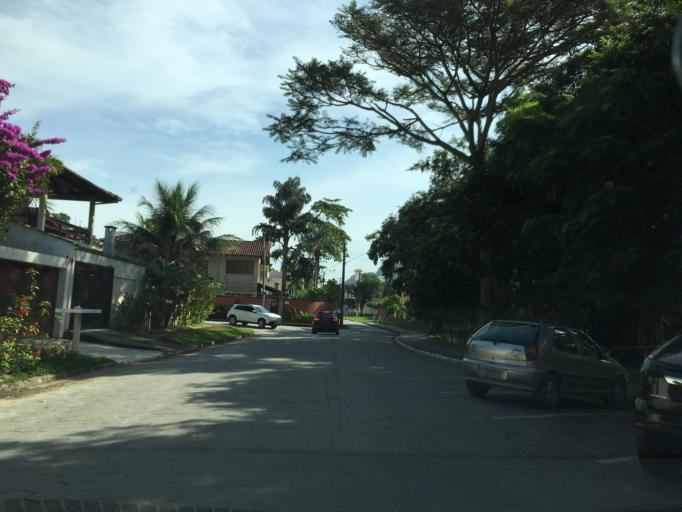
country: BR
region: Sao Paulo
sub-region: Sao Sebastiao
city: Sao Sebastiao
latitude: -23.7668
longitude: -45.7288
